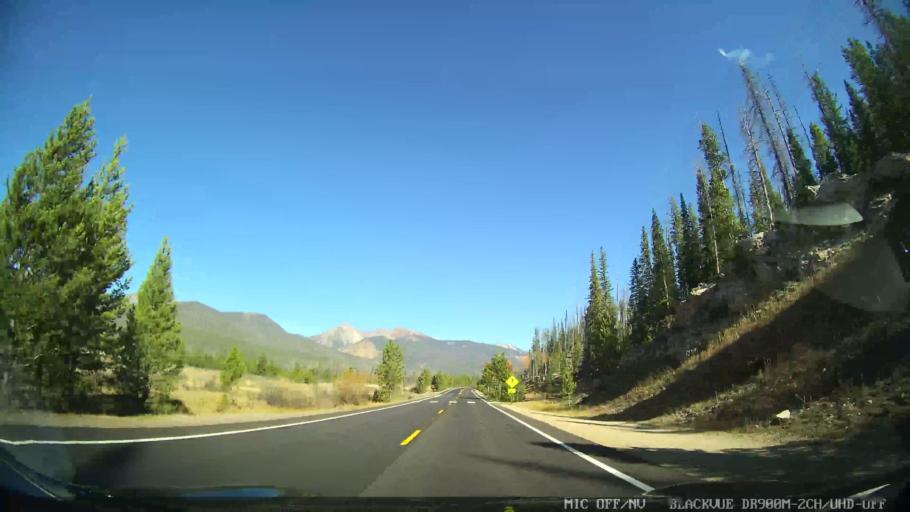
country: US
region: Colorado
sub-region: Grand County
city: Granby
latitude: 40.3250
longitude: -105.8530
